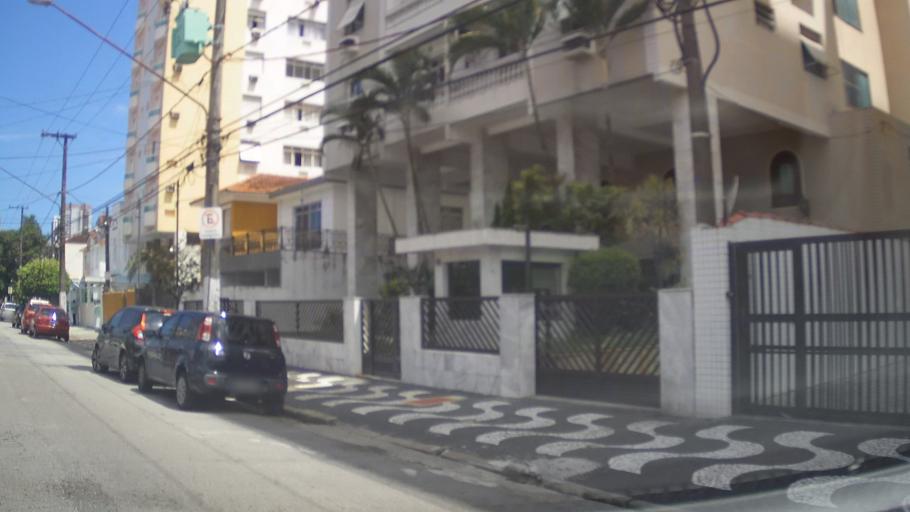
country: BR
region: Sao Paulo
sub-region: Santos
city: Santos
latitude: -23.9568
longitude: -46.3412
